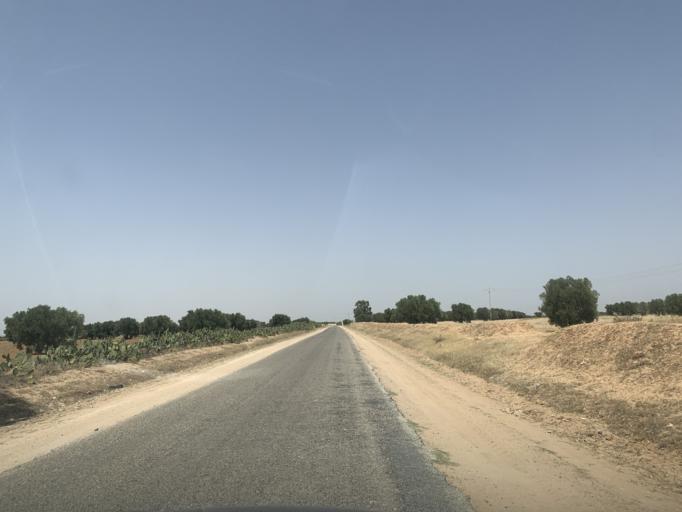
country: TN
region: Al Mahdiyah
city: Shurban
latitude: 35.1781
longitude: 10.2345
